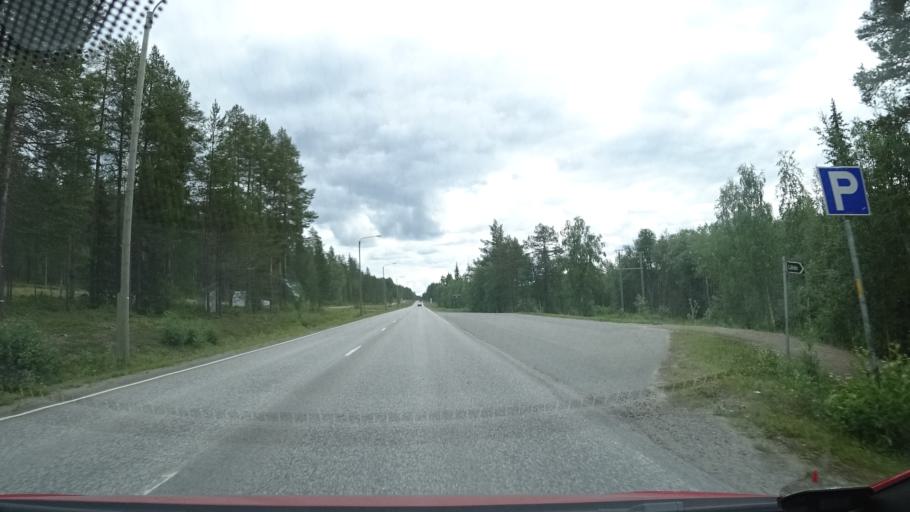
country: FI
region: Lapland
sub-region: Tunturi-Lappi
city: Kittilae
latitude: 67.7769
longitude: 24.8247
